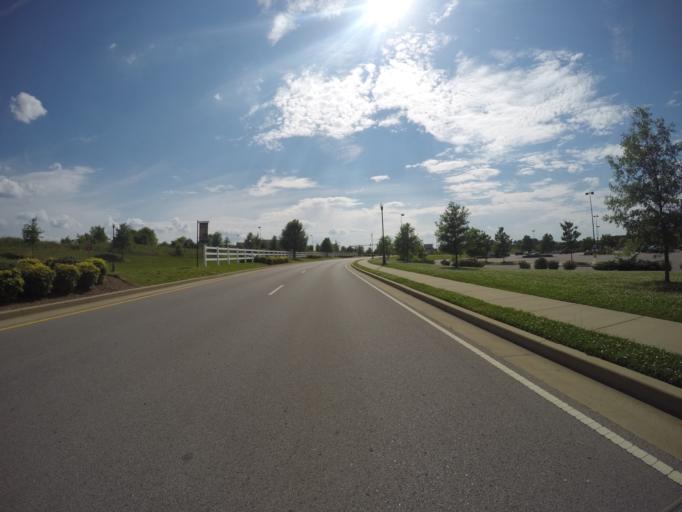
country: US
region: Tennessee
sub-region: Wilson County
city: Mount Juliet
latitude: 36.1773
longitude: -86.5180
